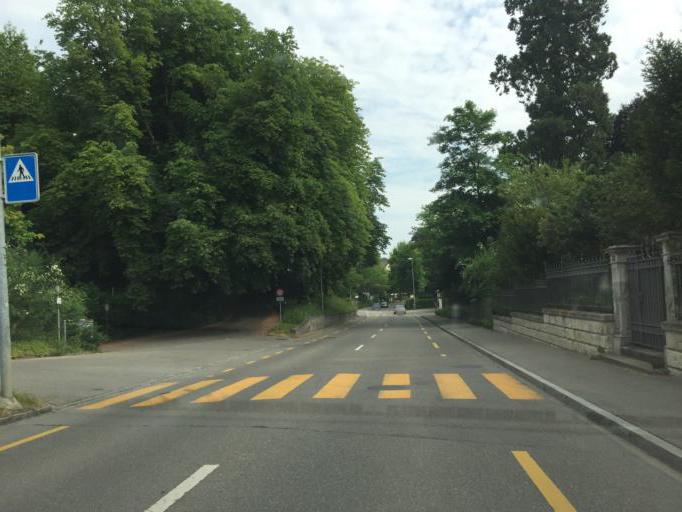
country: CH
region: Schaffhausen
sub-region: Bezirk Schaffhausen
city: Neuhausen
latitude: 47.6963
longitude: 8.6191
